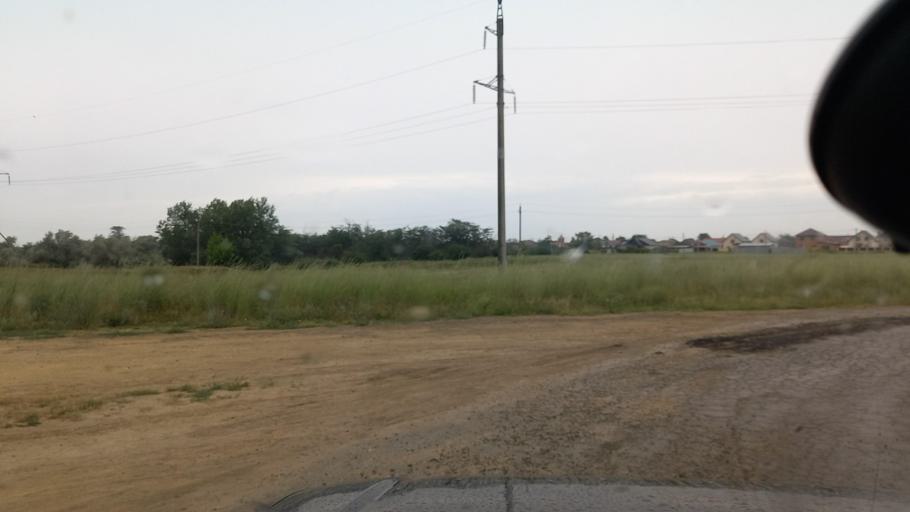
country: RU
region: Krasnodarskiy
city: Temryuk
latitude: 45.2558
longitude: 37.4369
